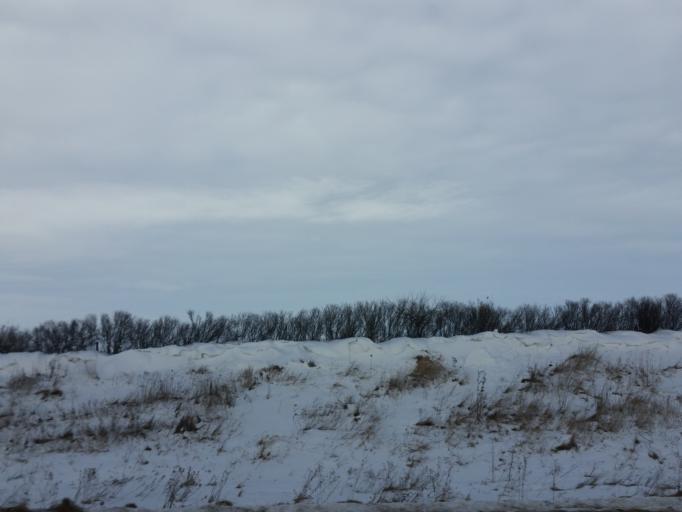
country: US
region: Iowa
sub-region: Delaware County
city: Manchester
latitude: 42.4646
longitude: -91.6049
